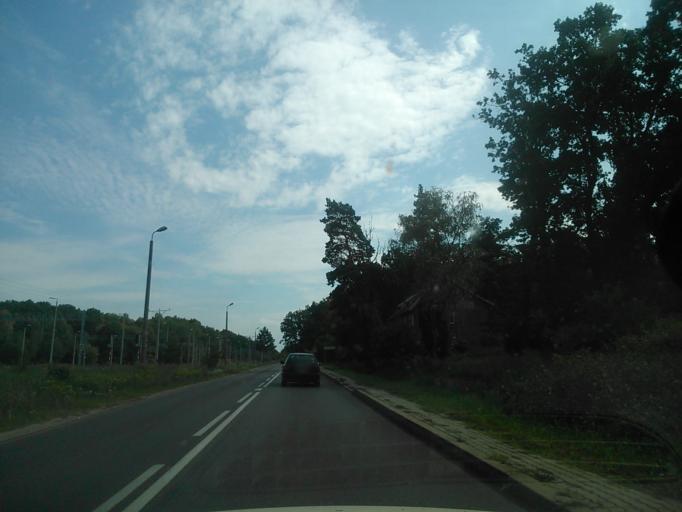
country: PL
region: Warmian-Masurian Voivodeship
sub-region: Powiat dzialdowski
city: Ilowo -Osada
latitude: 53.1602
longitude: 20.3045
